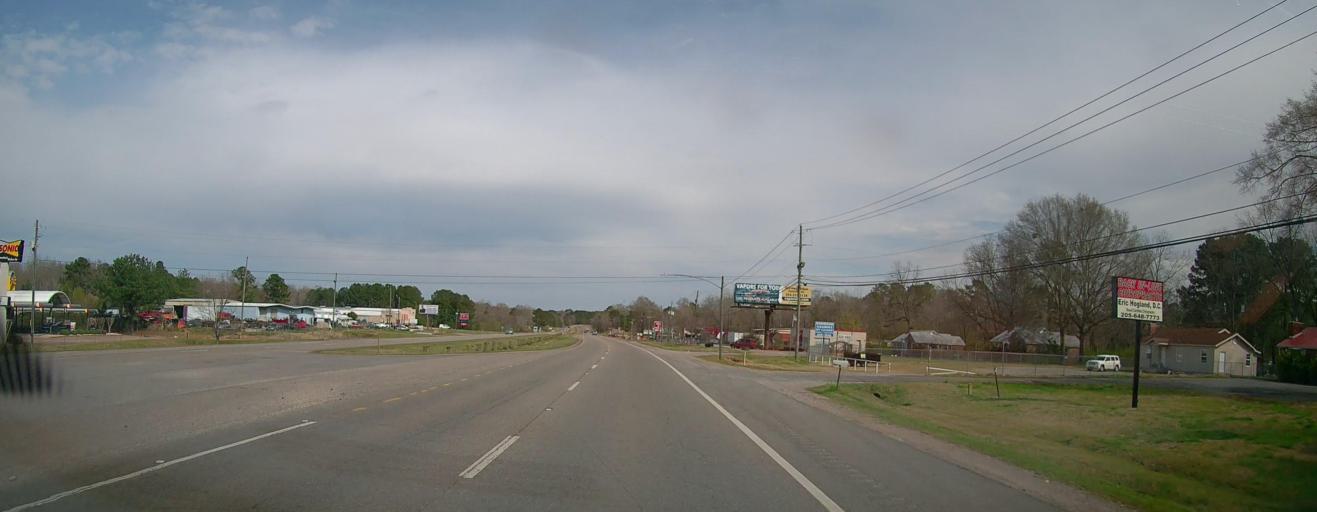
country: US
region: Alabama
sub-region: Walker County
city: Sumiton
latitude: 33.7416
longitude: -87.0390
